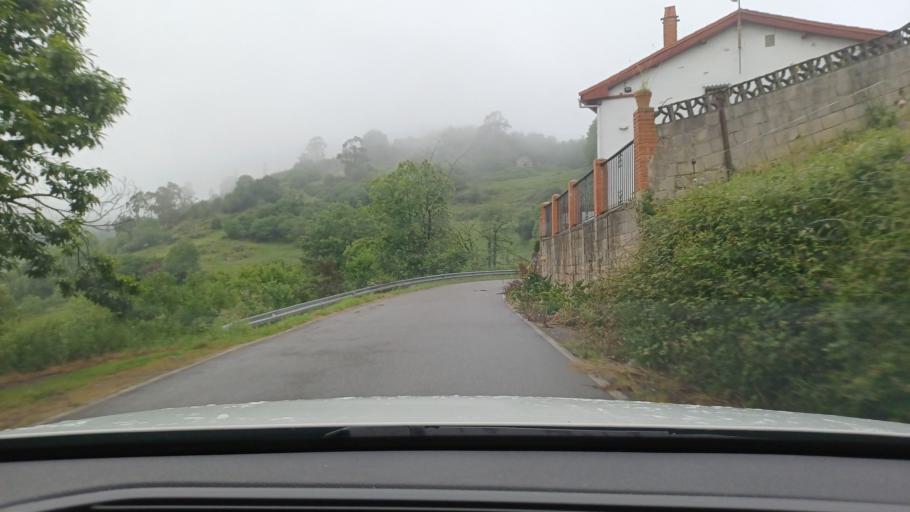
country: ES
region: Asturias
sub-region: Province of Asturias
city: Castandiello
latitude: 43.2984
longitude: -5.9533
